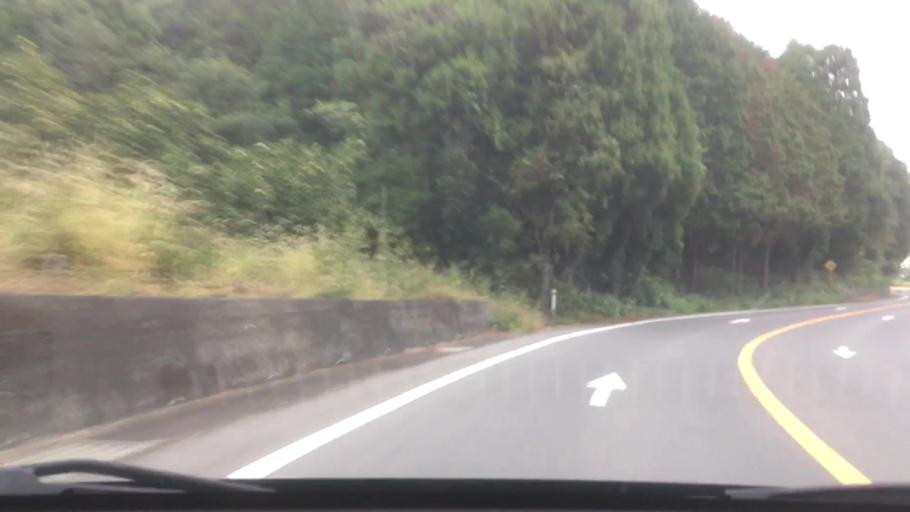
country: JP
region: Nagasaki
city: Sasebo
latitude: 33.0414
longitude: 129.6928
